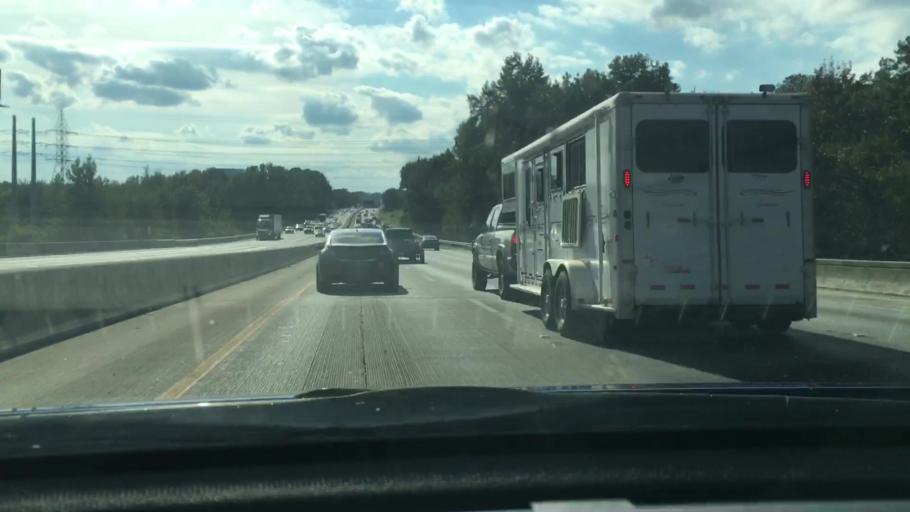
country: US
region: South Carolina
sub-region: Richland County
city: Columbia
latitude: 34.0539
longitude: -81.0597
